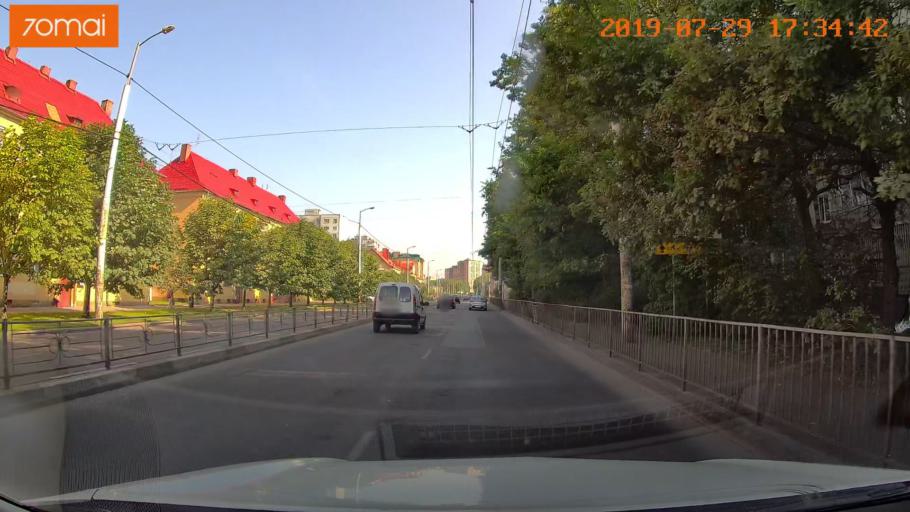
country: RU
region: Kaliningrad
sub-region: Gorod Kaliningrad
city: Kaliningrad
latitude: 54.7386
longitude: 20.5059
